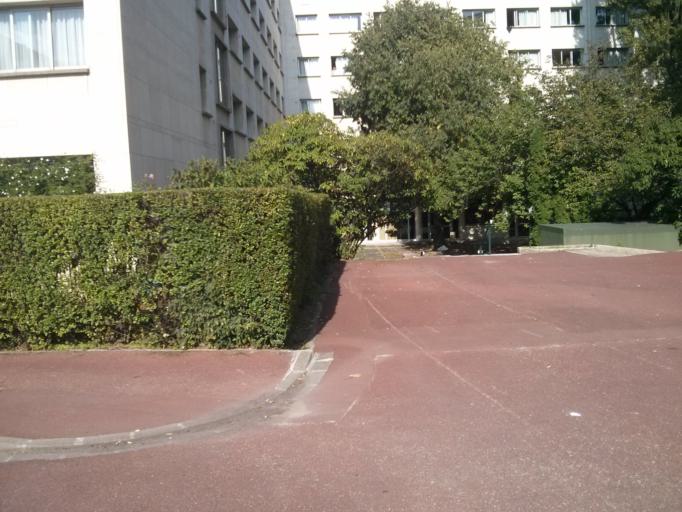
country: FR
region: Ile-de-France
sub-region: Departement du Val-de-Marne
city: Gentilly
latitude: 48.8208
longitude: 2.3329
